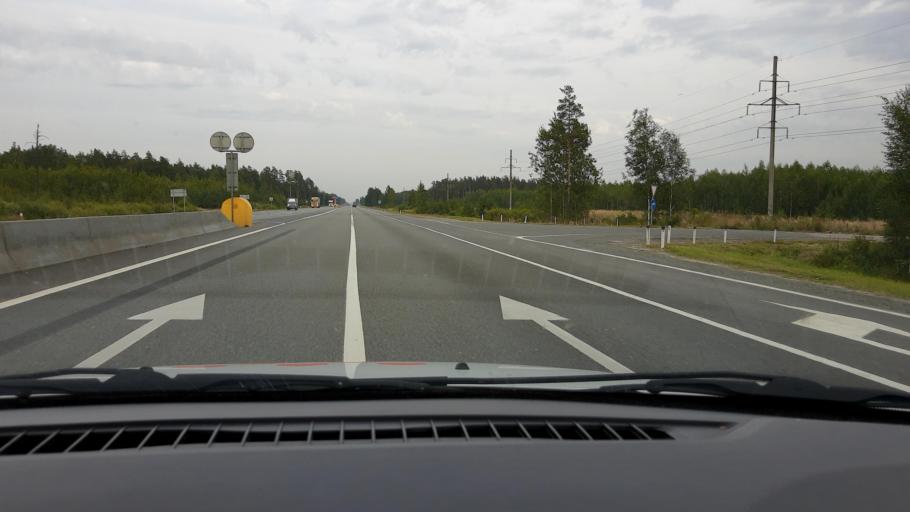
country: RU
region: Nizjnij Novgorod
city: Yuganets
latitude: 56.2889
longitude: 43.2678
